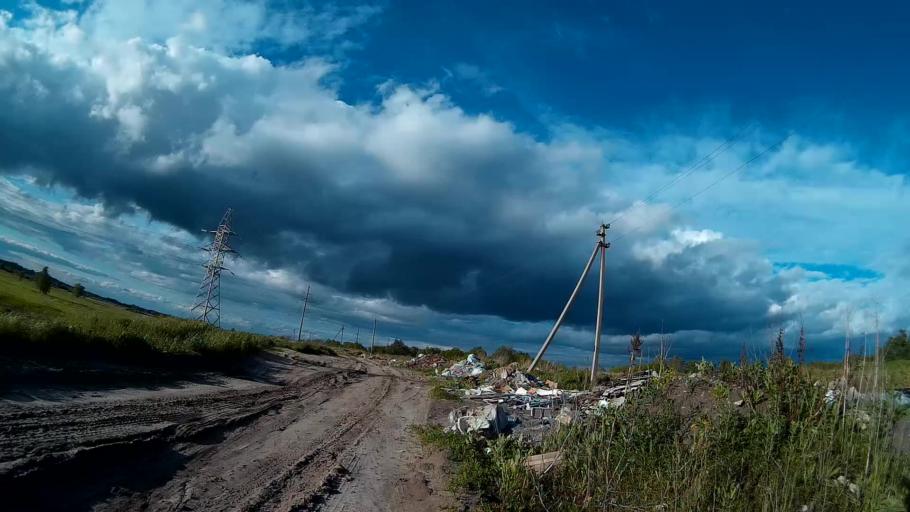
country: RU
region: Ulyanovsk
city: Novoul'yanovsk
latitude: 54.2101
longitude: 48.2767
